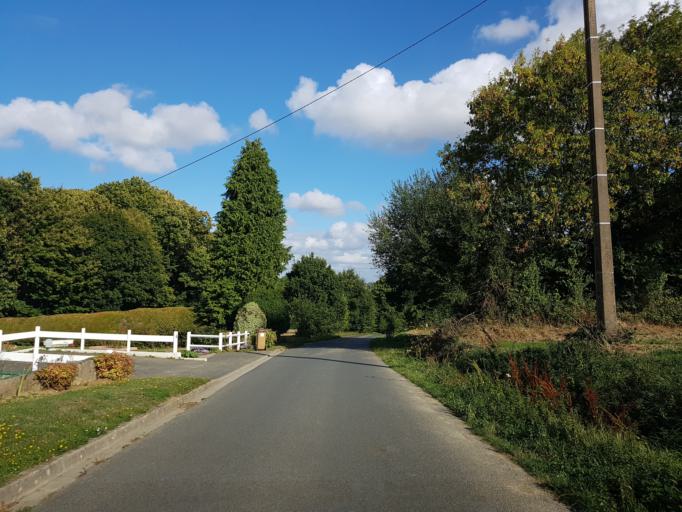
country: FR
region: Brittany
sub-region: Departement des Cotes-d'Armor
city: Pledran
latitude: 48.4675
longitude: -2.7575
